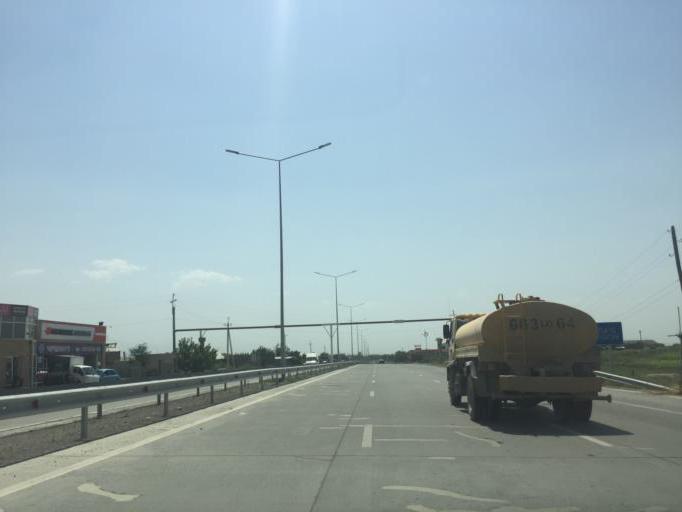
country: AM
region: Ararat
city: Norabats'
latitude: 40.1078
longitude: 44.4703
